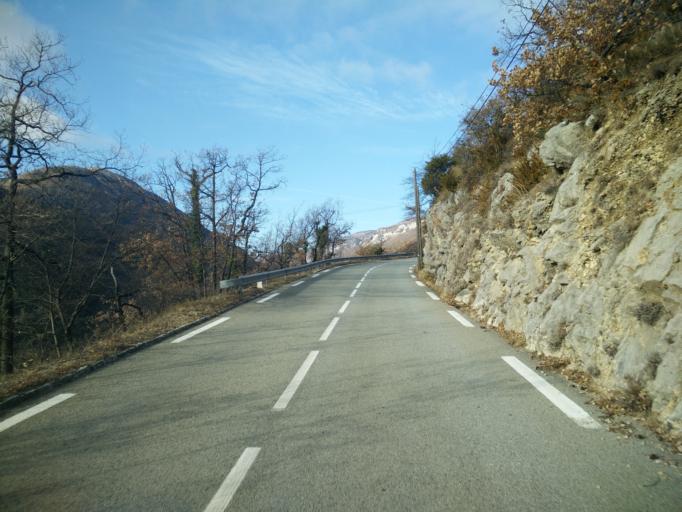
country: FR
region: Provence-Alpes-Cote d'Azur
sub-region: Departement des Alpes-Maritimes
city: Tourrettes-sur-Loup
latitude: 43.7885
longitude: 6.9720
